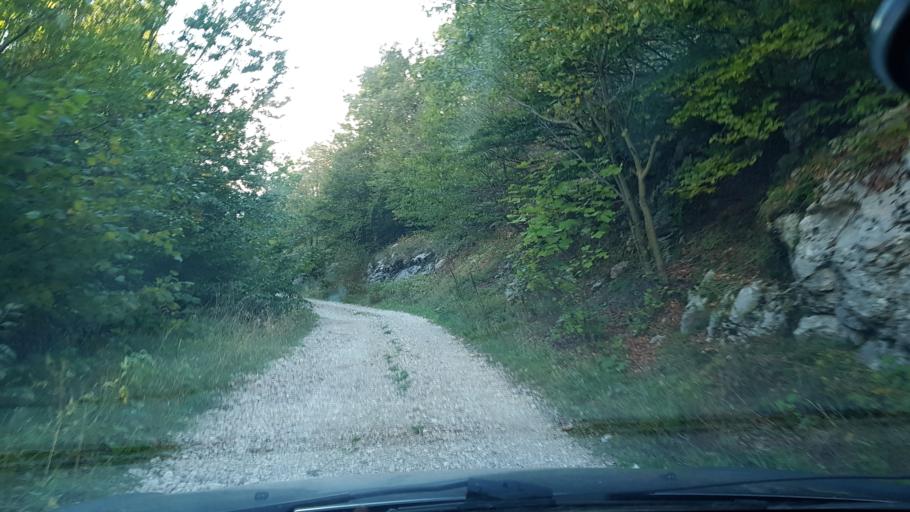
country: SI
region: Kobarid
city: Kobarid
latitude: 46.2804
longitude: 13.6285
